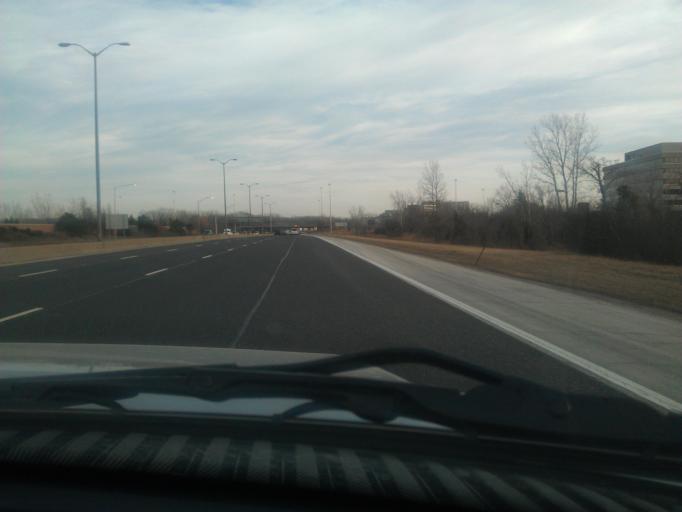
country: US
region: Illinois
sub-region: Cook County
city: Glencoe
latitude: 42.1427
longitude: -87.7923
